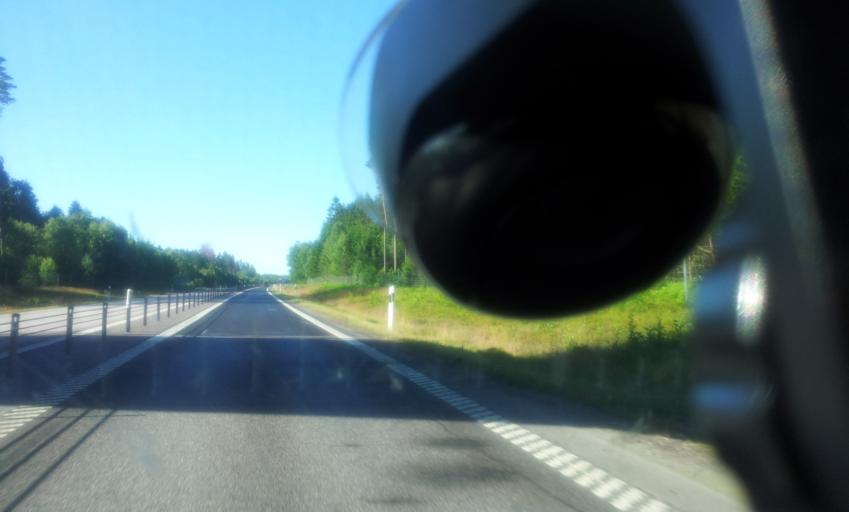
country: SE
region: Kalmar
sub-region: Torsas Kommun
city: Torsas
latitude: 56.5121
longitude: 16.0861
